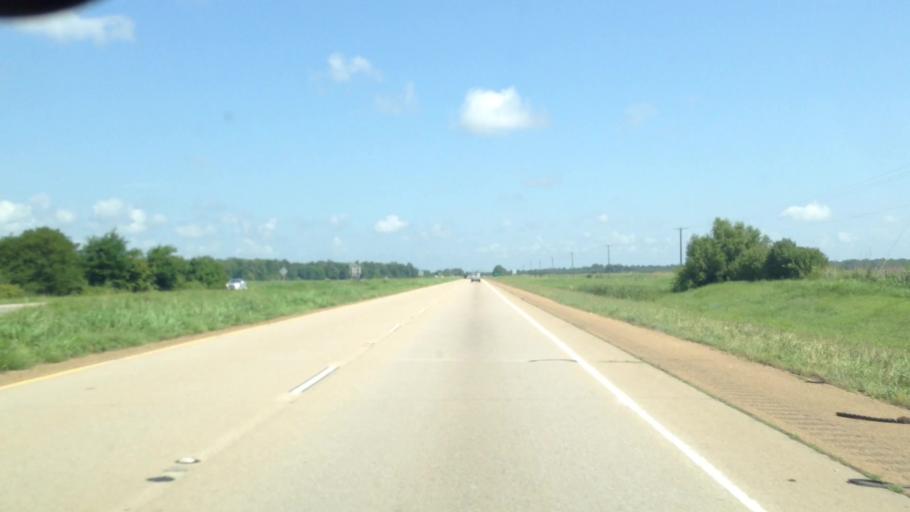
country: US
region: Louisiana
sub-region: Rapides Parish
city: Woodworth
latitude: 31.1727
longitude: -92.4641
